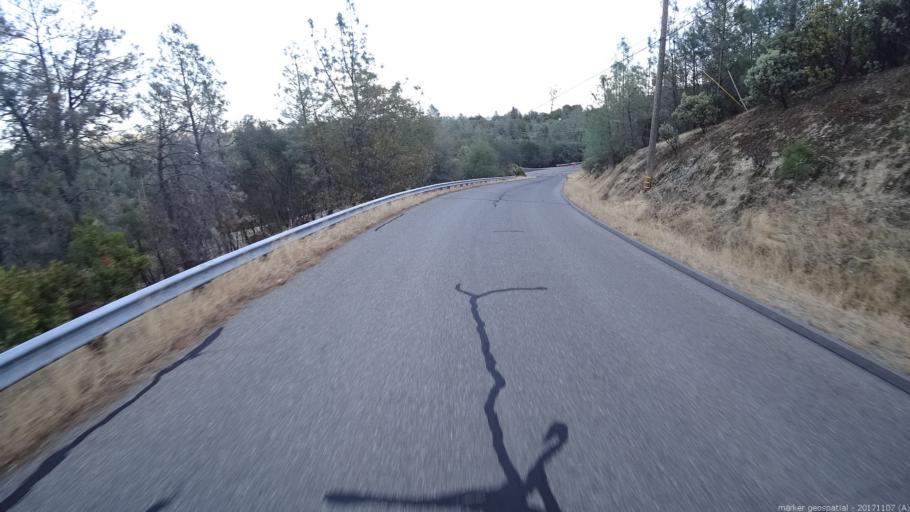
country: US
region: California
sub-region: Shasta County
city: Shasta
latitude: 40.5396
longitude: -122.4924
